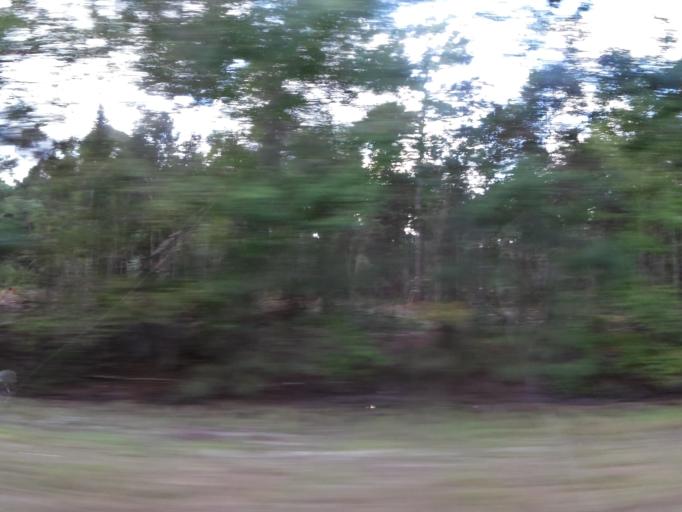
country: US
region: Georgia
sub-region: Liberty County
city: Midway
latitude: 31.6802
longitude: -81.4051
